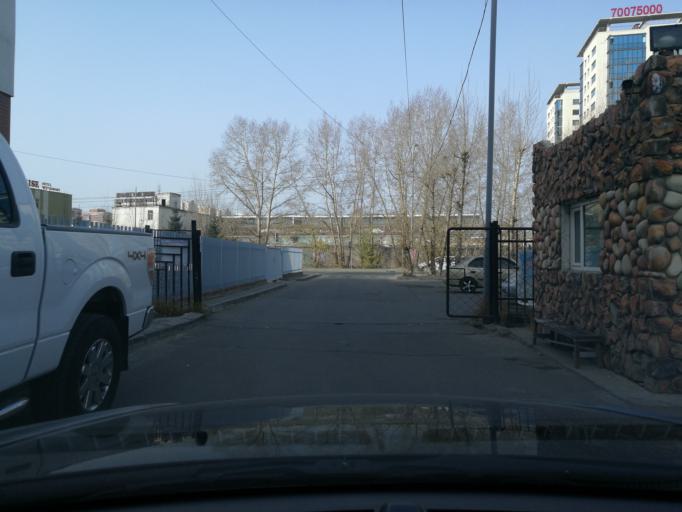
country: MN
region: Ulaanbaatar
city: Ulaanbaatar
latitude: 47.9092
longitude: 106.9081
